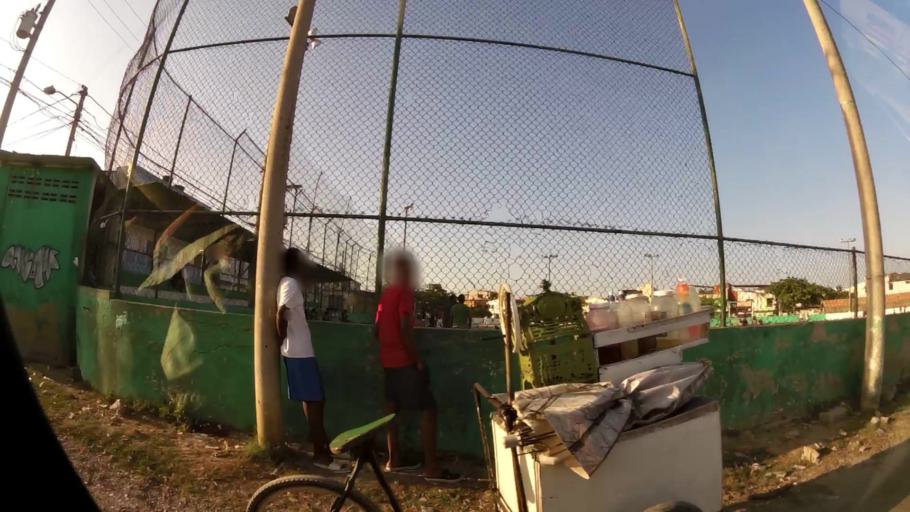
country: CO
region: Bolivar
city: Cartagena
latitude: 10.3992
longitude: -75.4718
